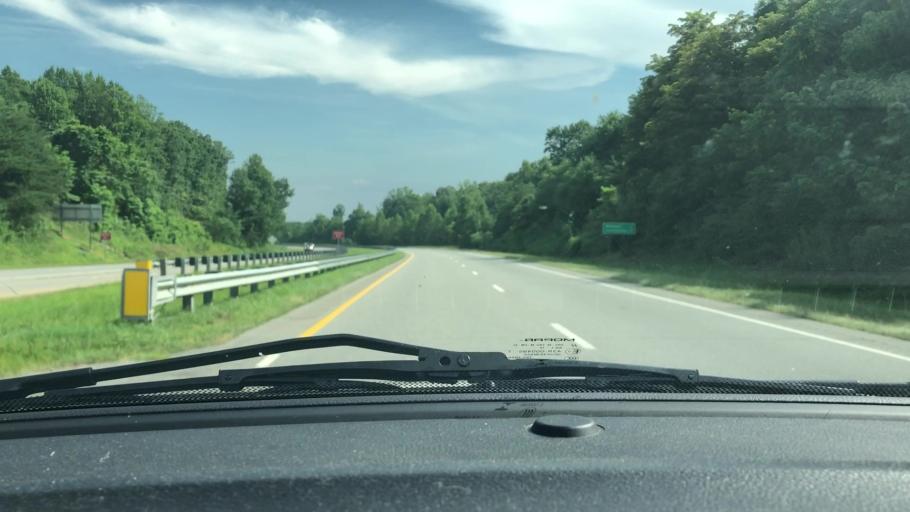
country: US
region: North Carolina
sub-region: Rockingham County
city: Stoneville
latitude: 36.4927
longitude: -79.9245
